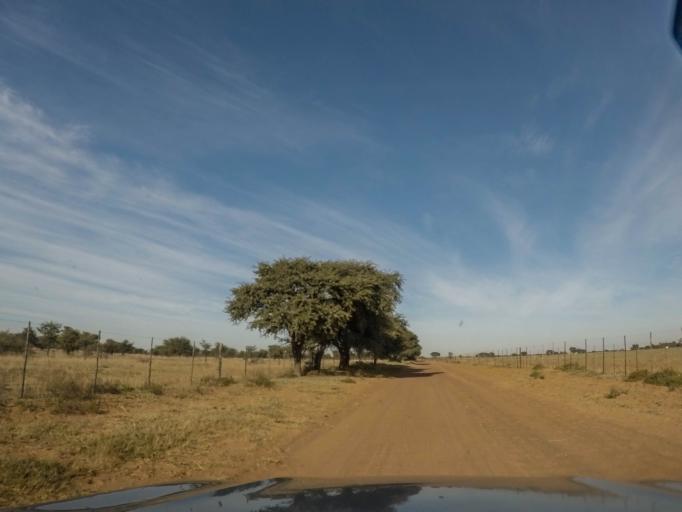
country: BW
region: South East
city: Janeng
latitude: -25.6546
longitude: 25.2525
